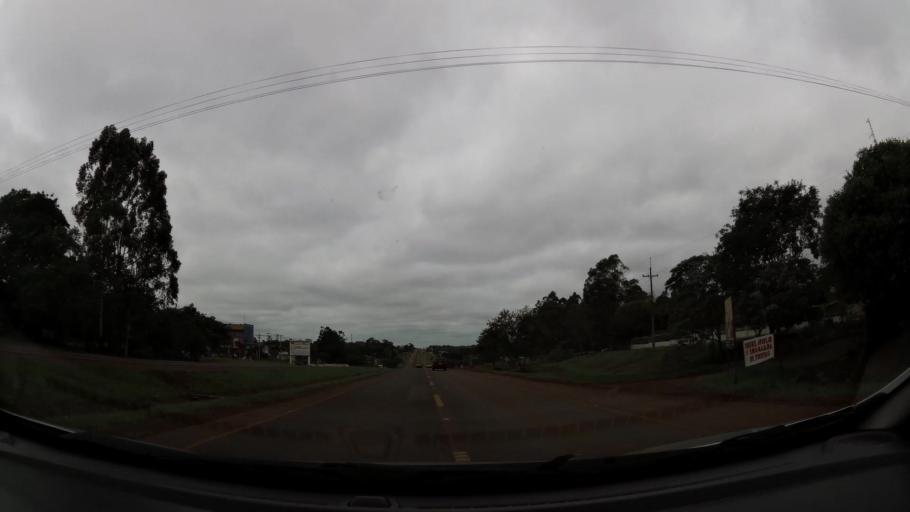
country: PY
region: Alto Parana
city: Los Cedrales
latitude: -25.4892
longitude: -54.8049
